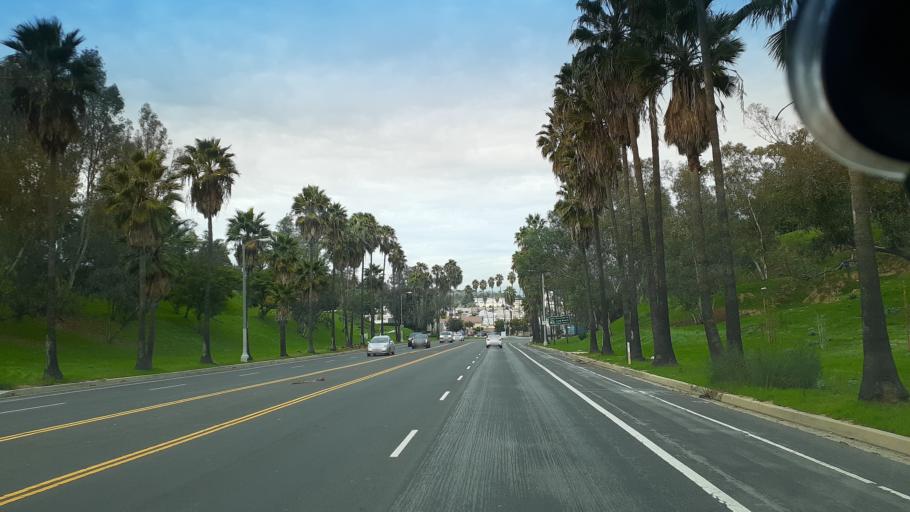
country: US
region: California
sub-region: Los Angeles County
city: San Pedro
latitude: 33.7501
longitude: -118.2933
